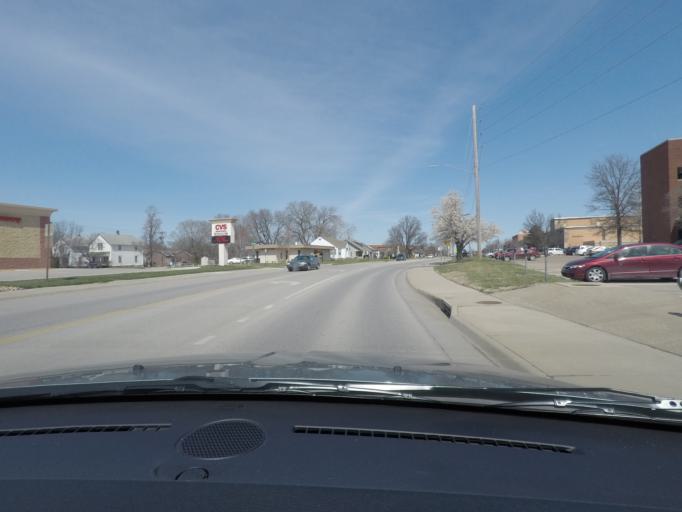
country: US
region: Kansas
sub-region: Lyon County
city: Emporia
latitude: 38.4129
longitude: -96.1818
